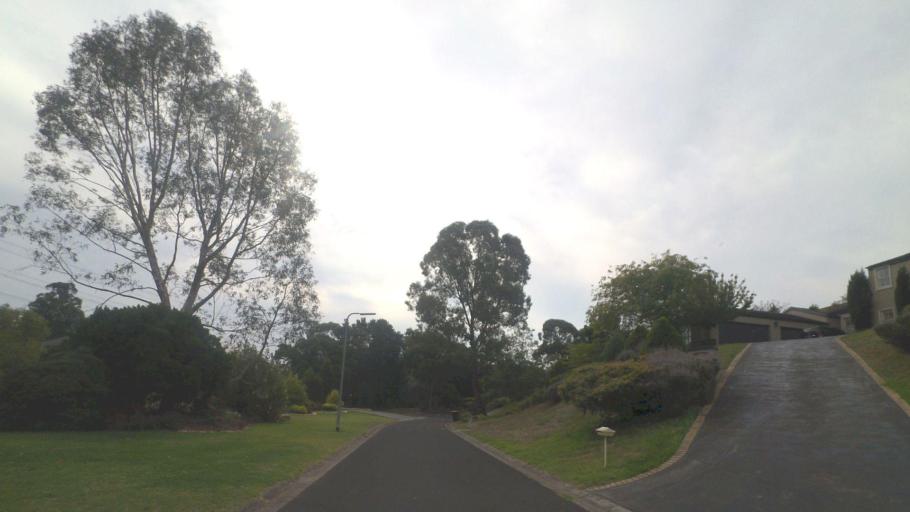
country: AU
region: Victoria
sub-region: Manningham
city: Park Orchards
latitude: -37.7633
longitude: 145.1914
